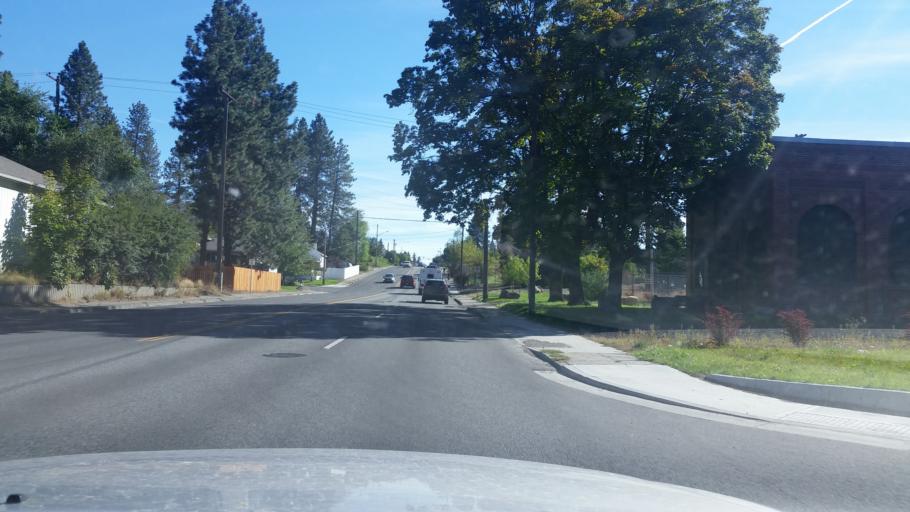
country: US
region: Washington
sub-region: Spokane County
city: Spokane
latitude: 47.6337
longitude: -117.3632
